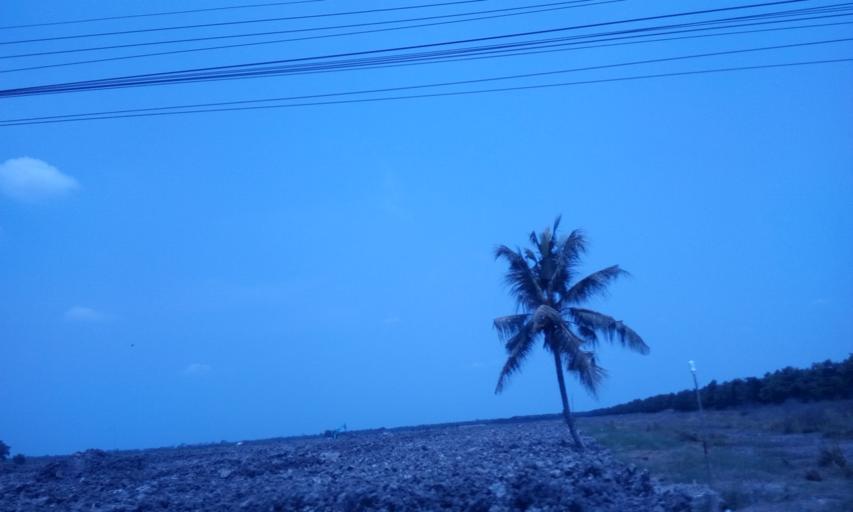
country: TH
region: Bangkok
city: Nong Chok
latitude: 13.9688
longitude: 100.9481
